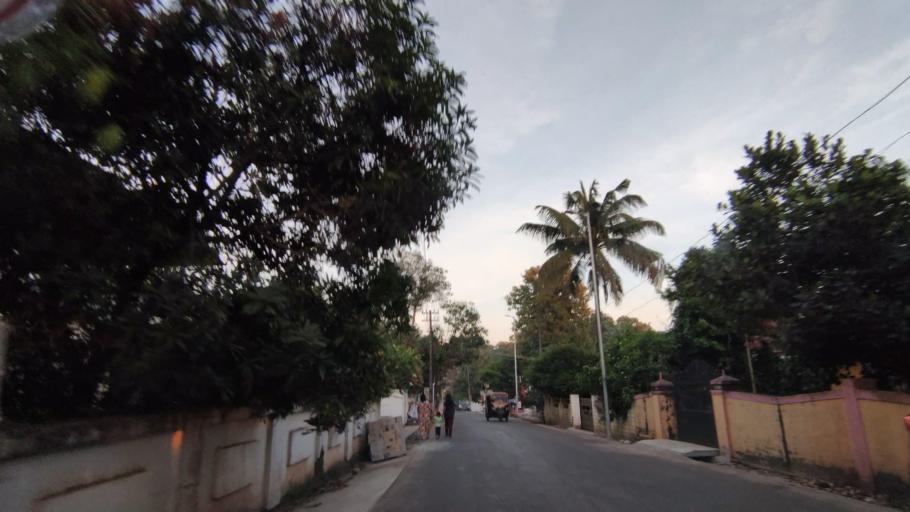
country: IN
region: Kerala
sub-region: Kottayam
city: Kottayam
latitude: 9.6420
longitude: 76.5046
